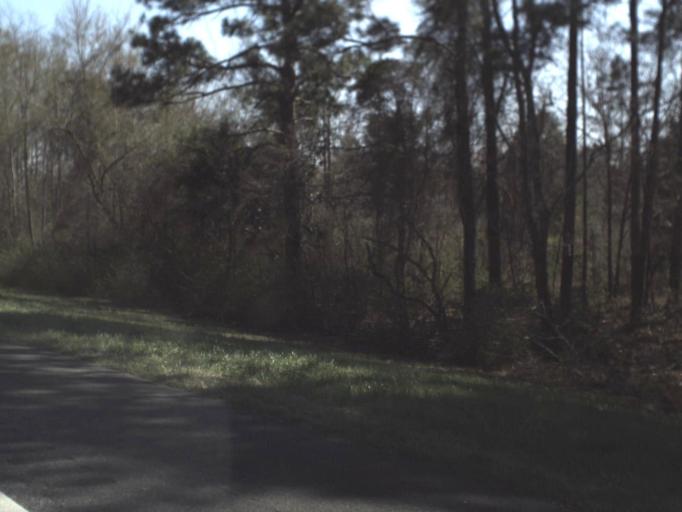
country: US
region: Florida
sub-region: Jackson County
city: Marianna
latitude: 30.7062
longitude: -85.1458
